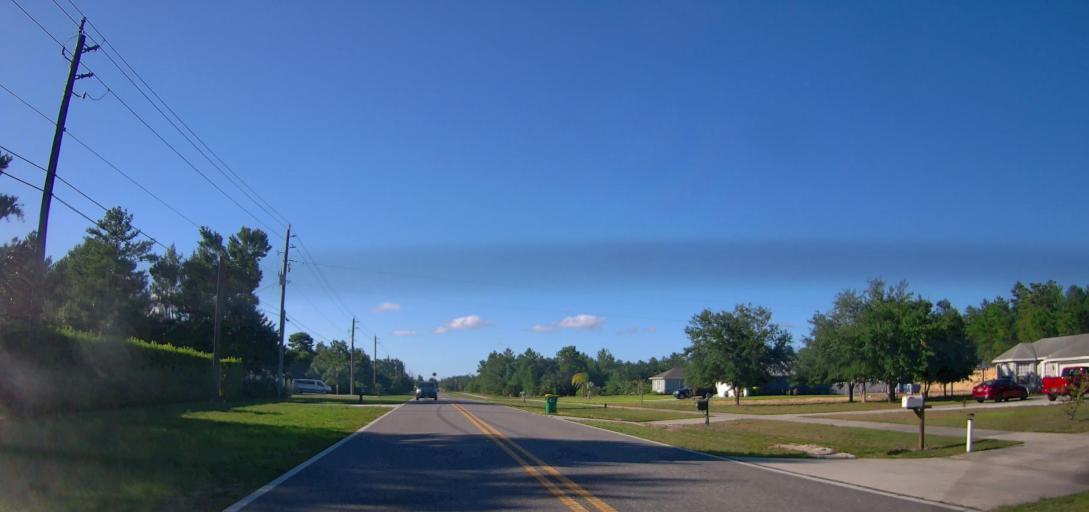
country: US
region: Florida
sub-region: Brevard County
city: Titusville
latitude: 28.5469
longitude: -80.8227
